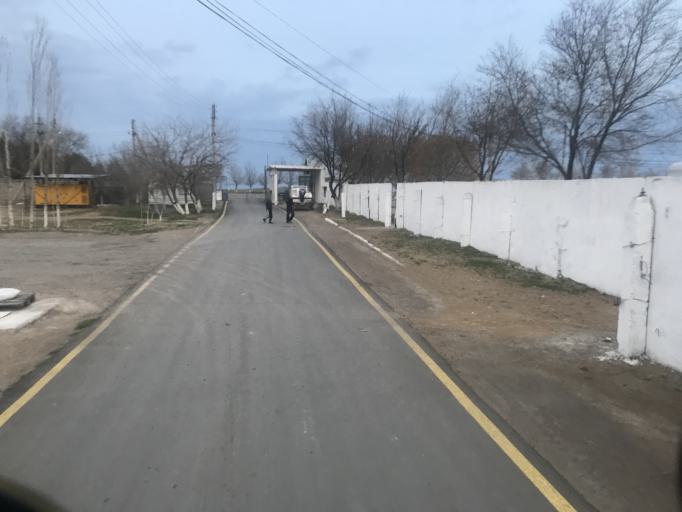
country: KZ
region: Ongtustik Qazaqstan
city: Shardara
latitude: 41.2497
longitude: 67.9010
